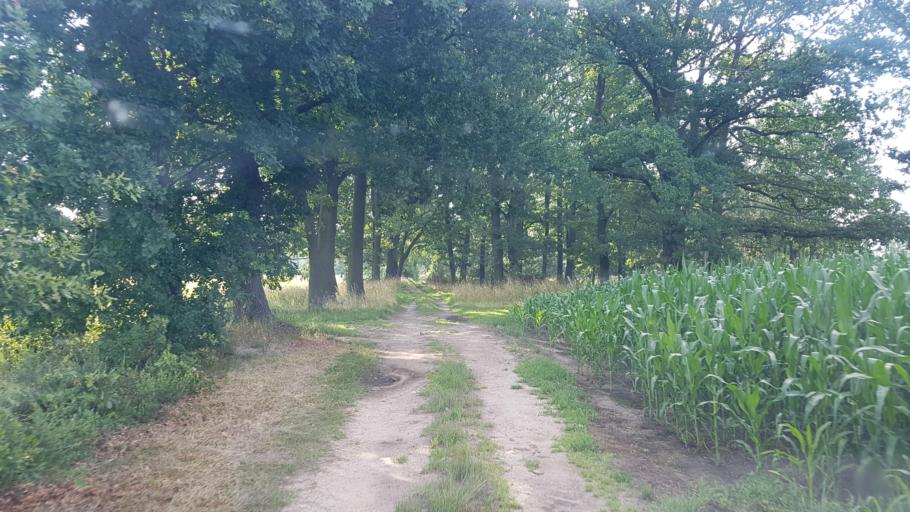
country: DE
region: Brandenburg
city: Finsterwalde
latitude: 51.6754
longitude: 13.7319
